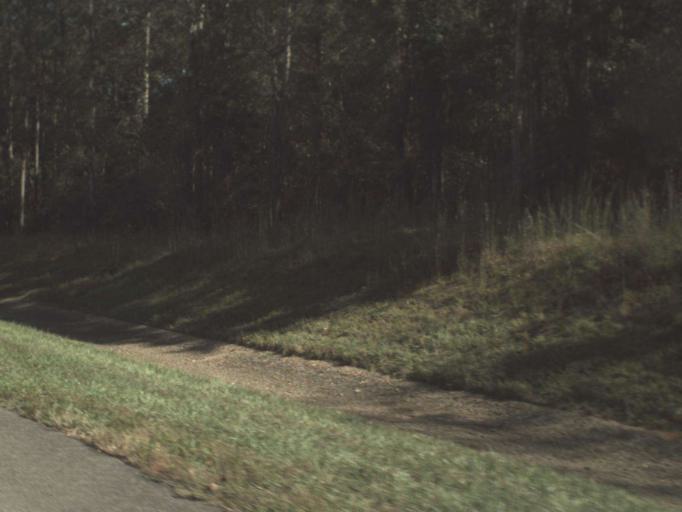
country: US
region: Florida
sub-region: Walton County
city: DeFuniak Springs
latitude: 30.6039
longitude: -85.9418
